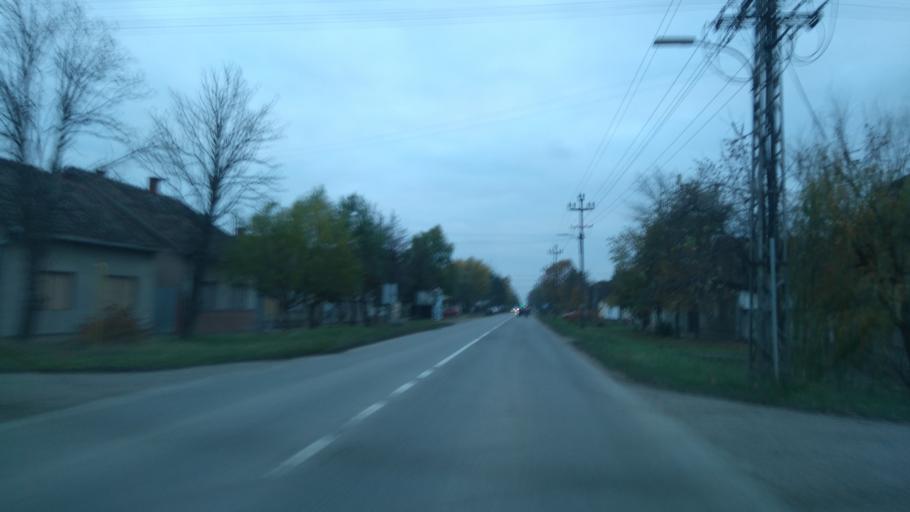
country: RS
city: Mol
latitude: 45.7706
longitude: 20.1287
